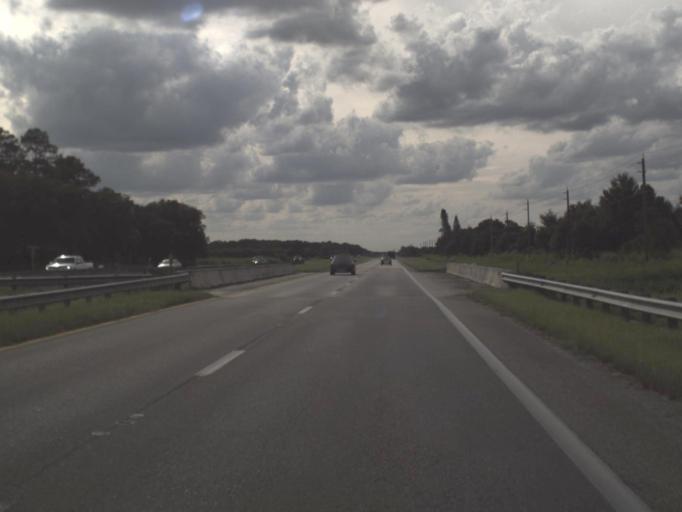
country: US
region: Florida
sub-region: Lee County
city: Alva
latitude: 26.7097
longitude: -81.5577
